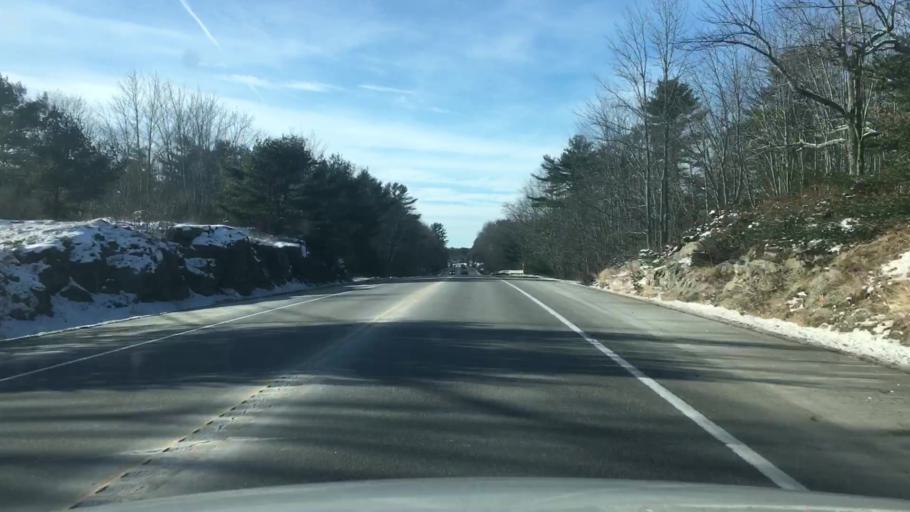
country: US
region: Maine
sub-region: Sagadahoc County
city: Woolwich
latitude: 43.9407
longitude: -69.7652
